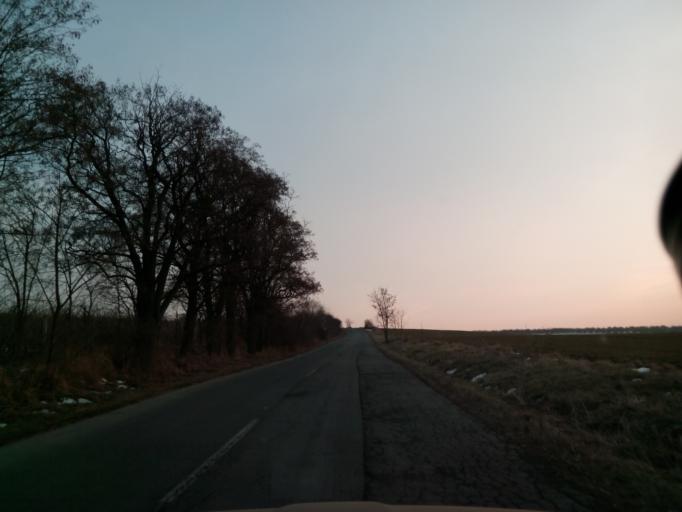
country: HU
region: Borsod-Abauj-Zemplen
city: Gonc
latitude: 48.4948
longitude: 21.3004
